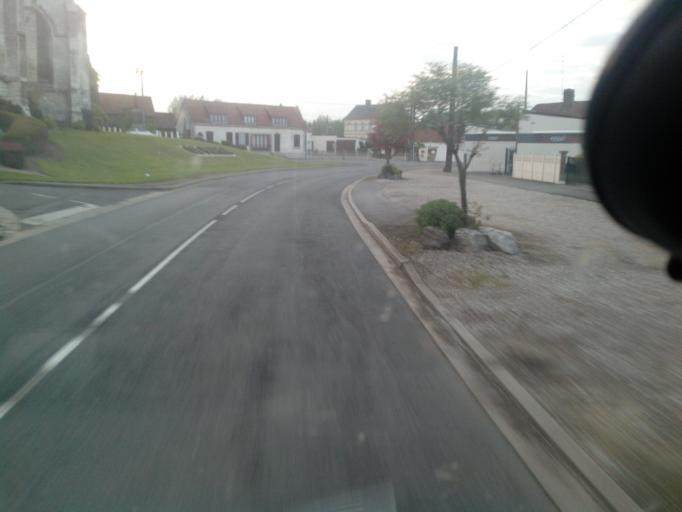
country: FR
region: Picardie
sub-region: Departement de la Somme
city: Crecy-en-Ponthieu
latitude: 50.2709
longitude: 1.9842
